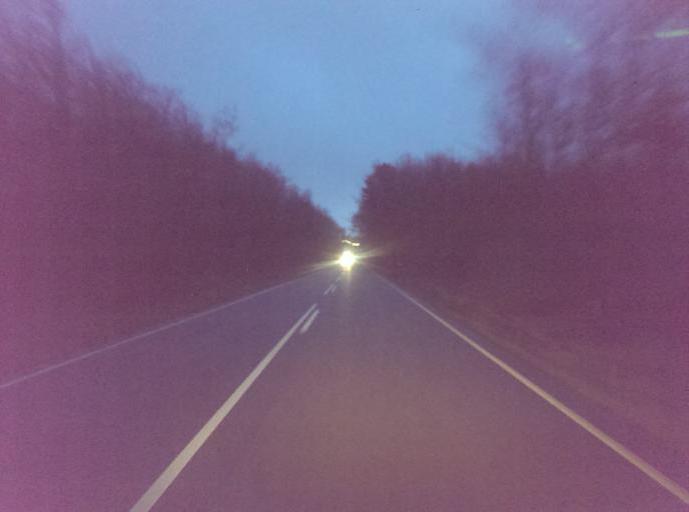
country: DK
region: South Denmark
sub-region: Esbjerg Kommune
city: Tjaereborg
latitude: 55.4810
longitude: 8.5791
